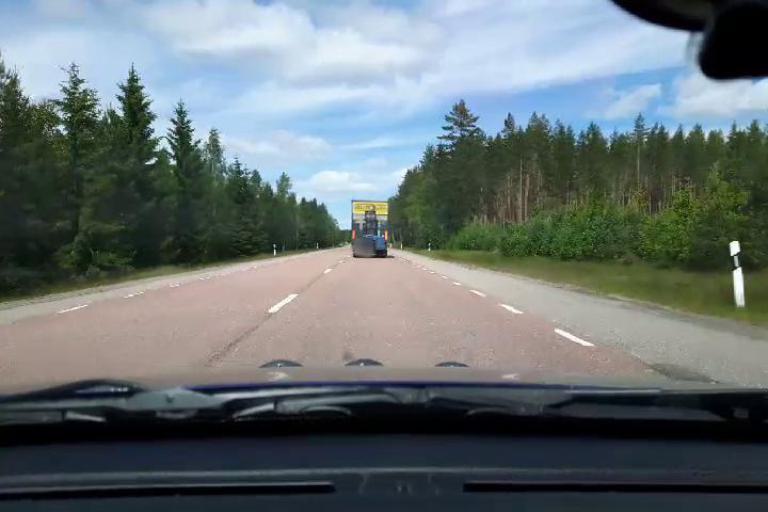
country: SE
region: Uppsala
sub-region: Osthammars Kommun
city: Bjorklinge
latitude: 60.1605
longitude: 17.4913
